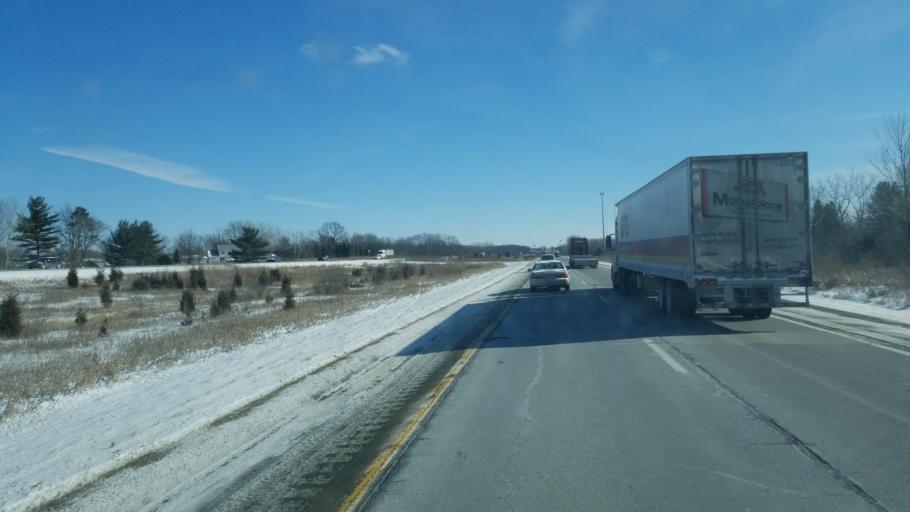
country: US
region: Michigan
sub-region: Livingston County
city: Fowlerville
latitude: 42.6347
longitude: -84.0233
